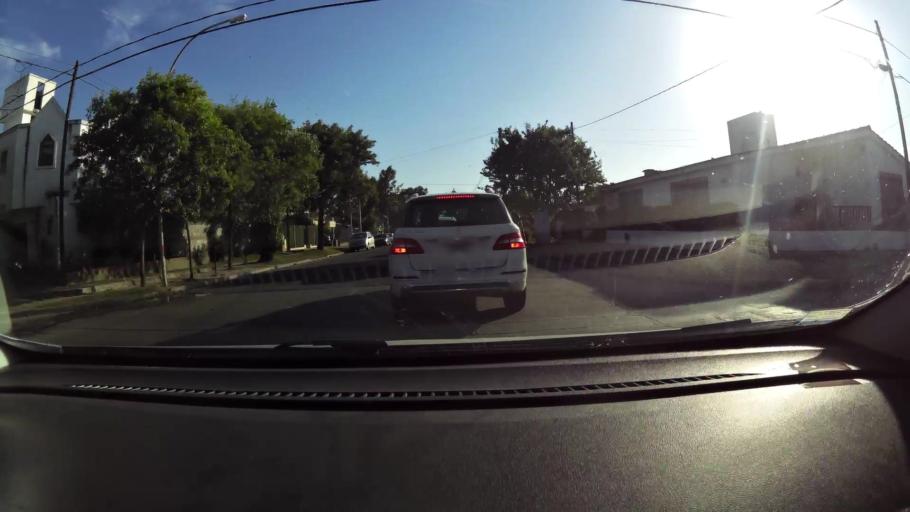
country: AR
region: Cordoba
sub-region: Departamento de Capital
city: Cordoba
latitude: -31.3785
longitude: -64.2434
